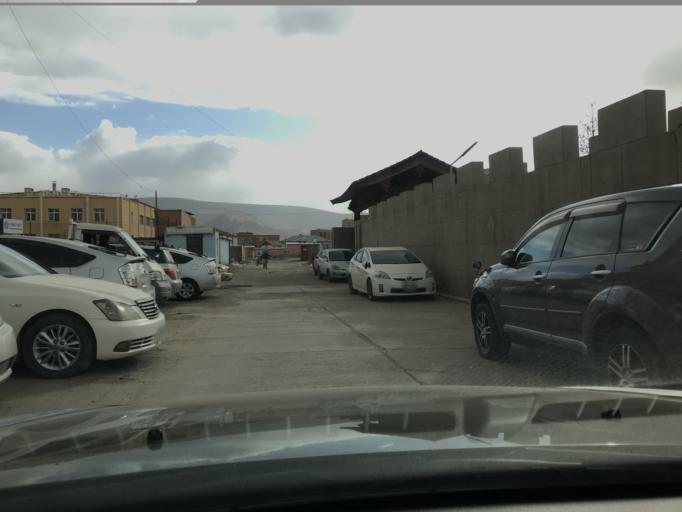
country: MN
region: Ulaanbaatar
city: Ulaanbaatar
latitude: 47.9129
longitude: 106.9742
